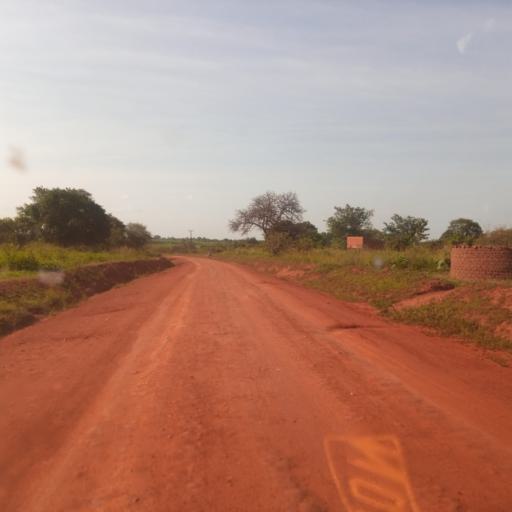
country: UG
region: Northern Region
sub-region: Kitgum District
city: Kitgum
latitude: 3.1115
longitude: 32.9147
